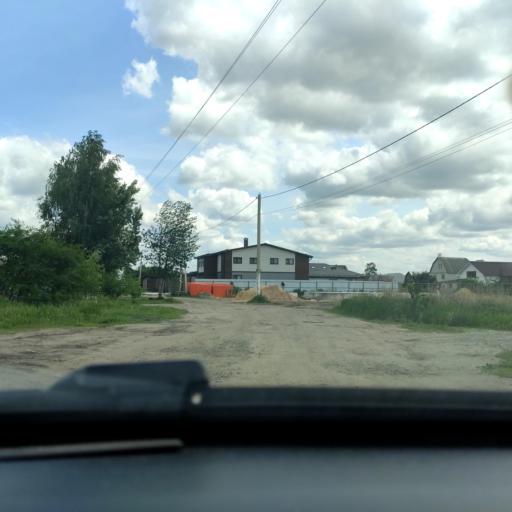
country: RU
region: Voronezj
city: Somovo
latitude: 51.6943
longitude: 39.3182
